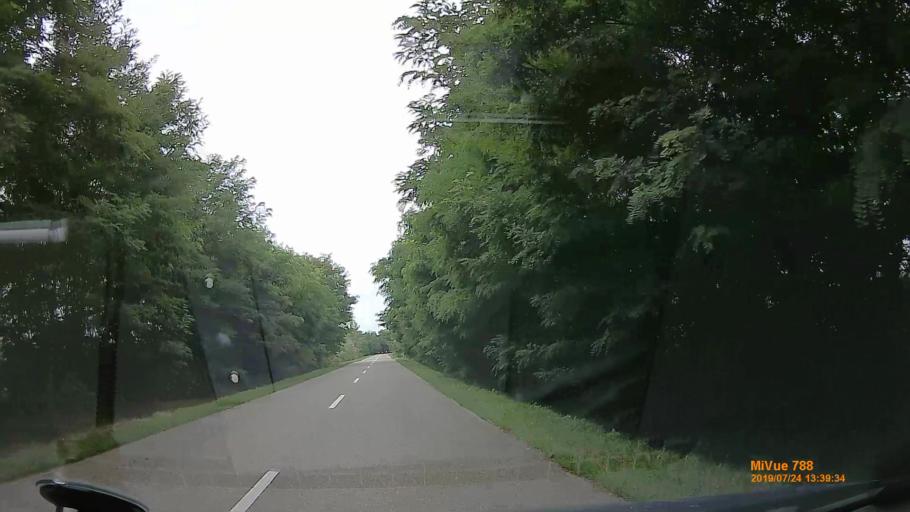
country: HU
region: Szabolcs-Szatmar-Bereg
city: Aranyosapati
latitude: 48.2413
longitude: 22.3183
